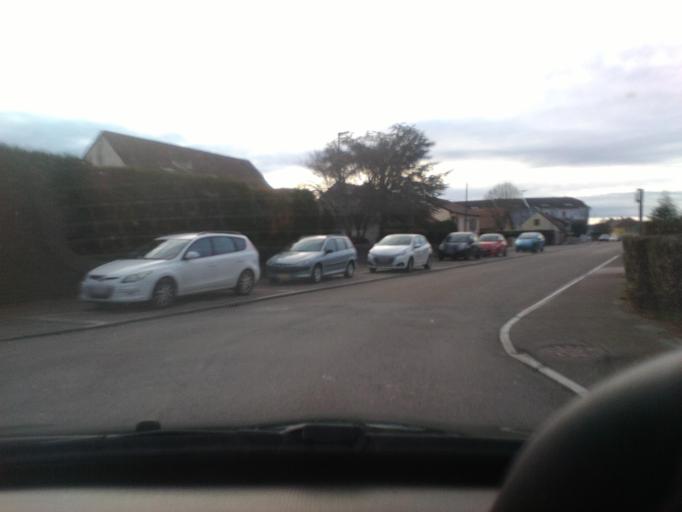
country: FR
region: Lorraine
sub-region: Departement des Vosges
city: Golbey
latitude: 48.2009
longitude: 6.4374
